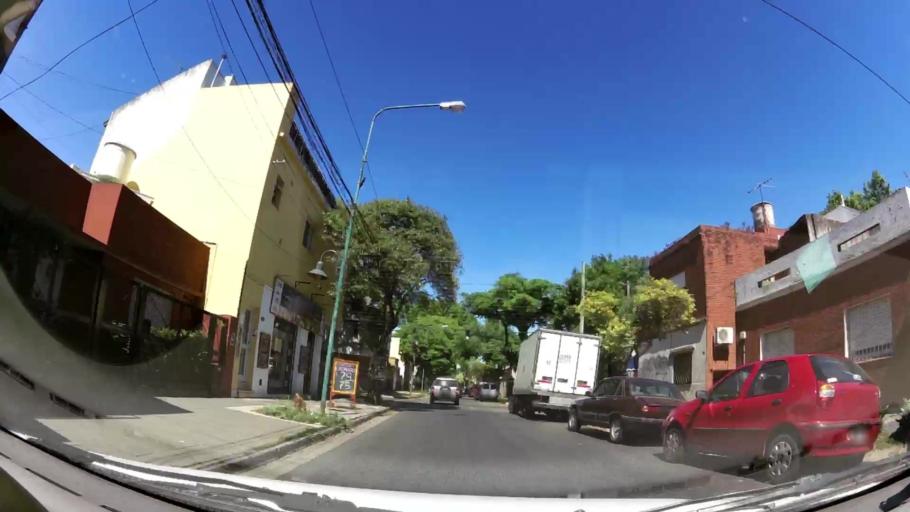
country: AR
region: Buenos Aires
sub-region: Partido de Vicente Lopez
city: Olivos
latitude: -34.5206
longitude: -58.4977
